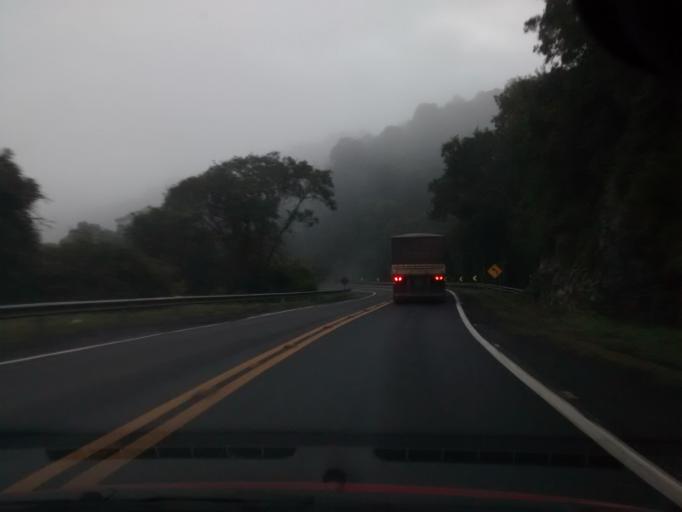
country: BR
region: Rio Grande do Sul
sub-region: Vacaria
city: Estrela
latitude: -28.1989
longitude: -50.7280
